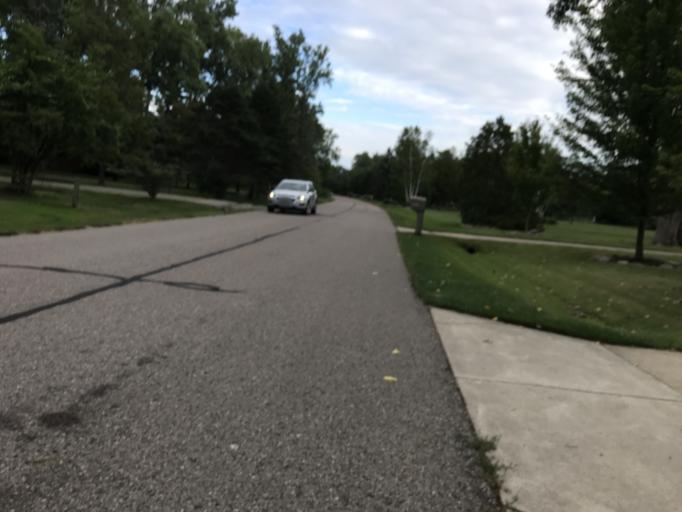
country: US
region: Michigan
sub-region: Oakland County
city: Farmington Hills
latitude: 42.4828
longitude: -83.3447
